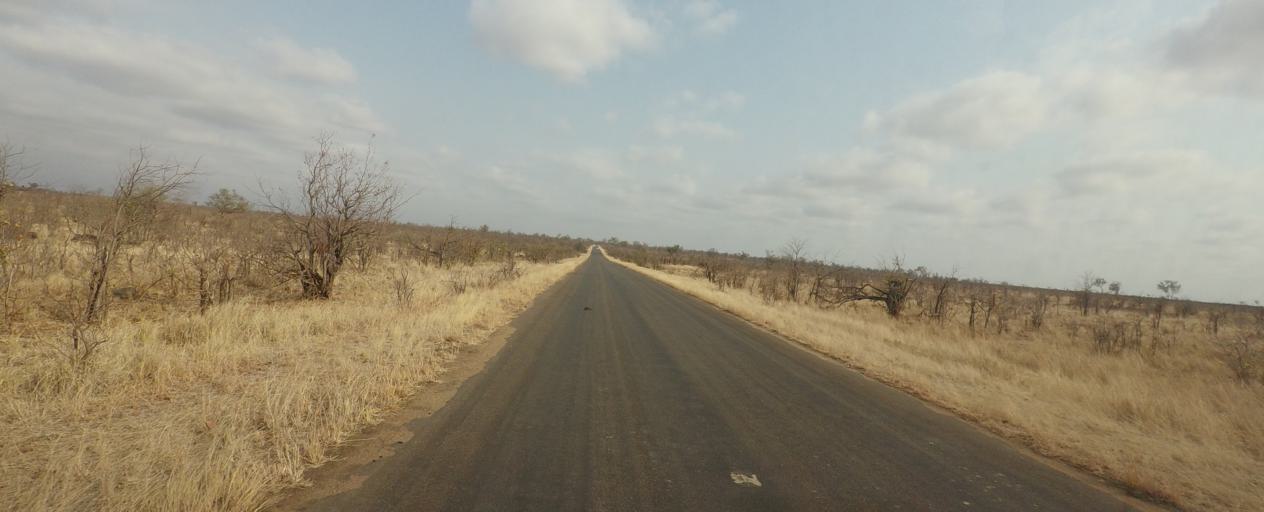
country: ZA
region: Limpopo
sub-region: Vhembe District Municipality
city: Mutale
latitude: -22.8954
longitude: 31.2503
